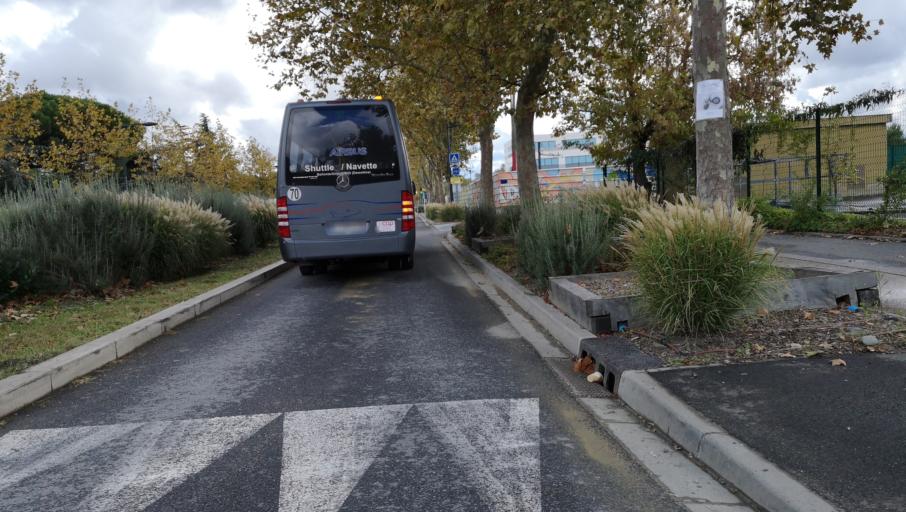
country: FR
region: Midi-Pyrenees
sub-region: Departement de la Haute-Garonne
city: Blagnac
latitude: 43.6296
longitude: 1.3796
